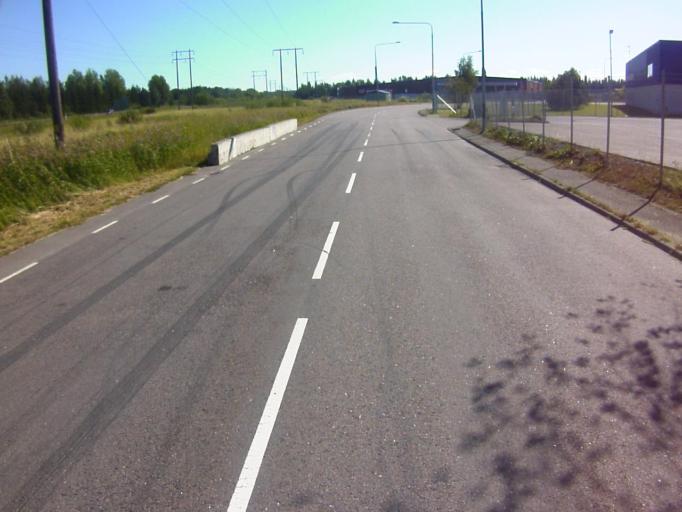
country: SE
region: Soedermanland
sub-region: Eskilstuna Kommun
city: Eskilstuna
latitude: 59.3886
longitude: 16.4871
